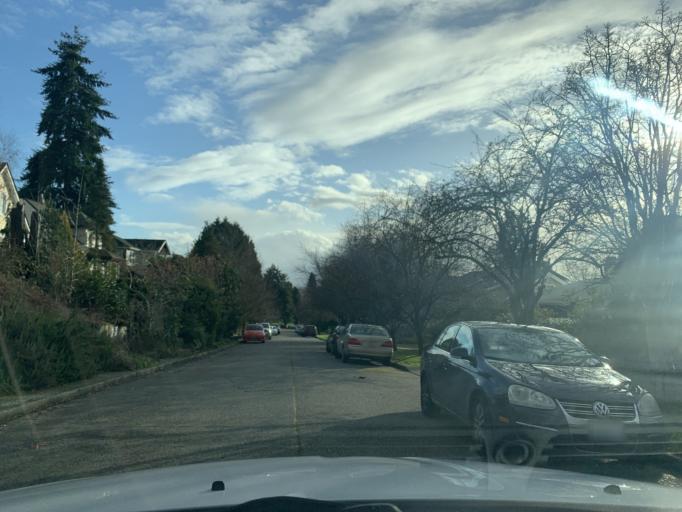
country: US
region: Washington
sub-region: King County
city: Seattle
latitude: 47.6701
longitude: -122.2939
